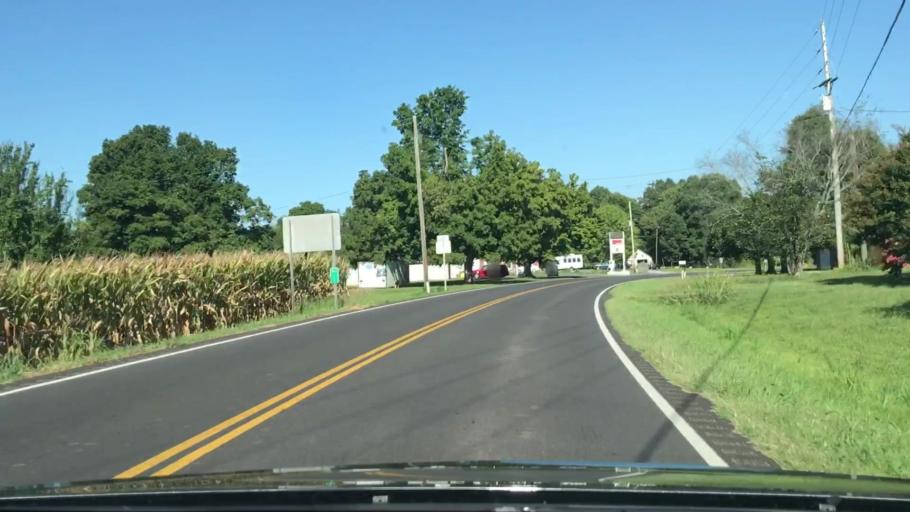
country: US
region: Kentucky
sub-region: Marshall County
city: Benton
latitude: 36.7687
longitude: -88.4376
